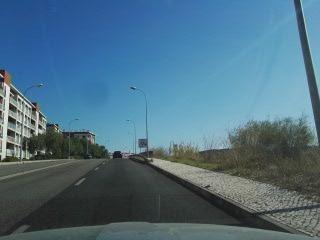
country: PT
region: Lisbon
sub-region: Oeiras
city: Alges
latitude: 38.7196
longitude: -9.2219
